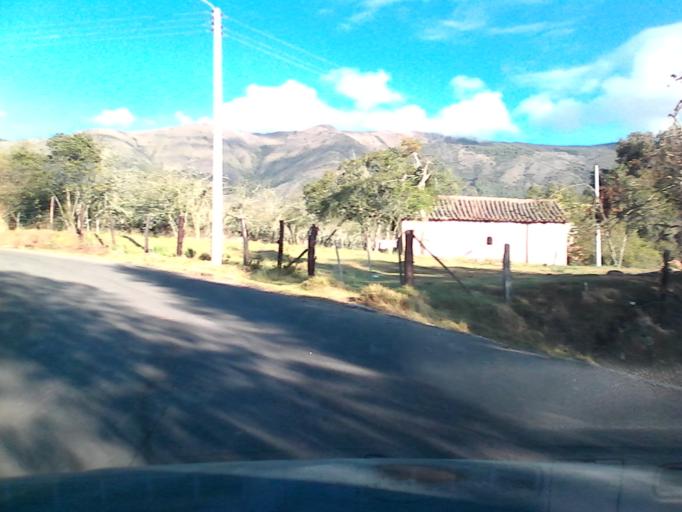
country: CO
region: Boyaca
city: Duitama
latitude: 5.8638
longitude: -73.0277
